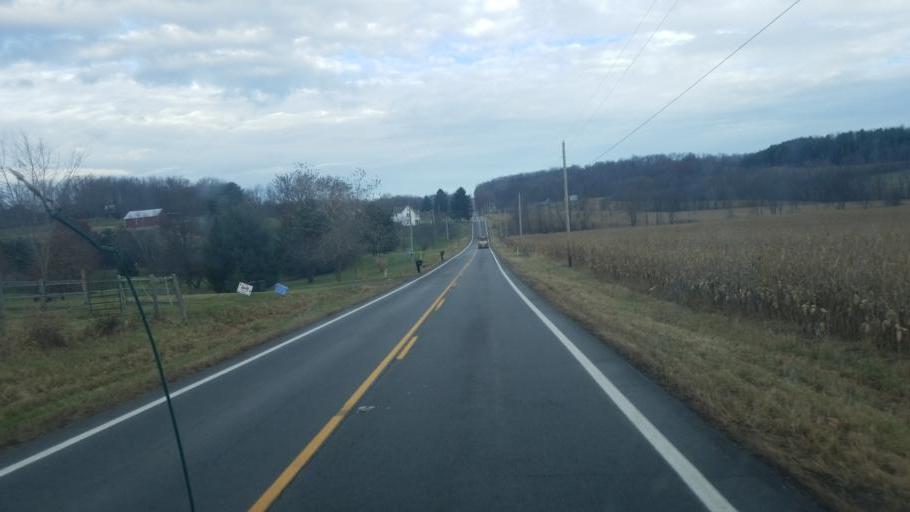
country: US
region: Ohio
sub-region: Sandusky County
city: Bellville
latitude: 40.6669
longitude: -82.3776
